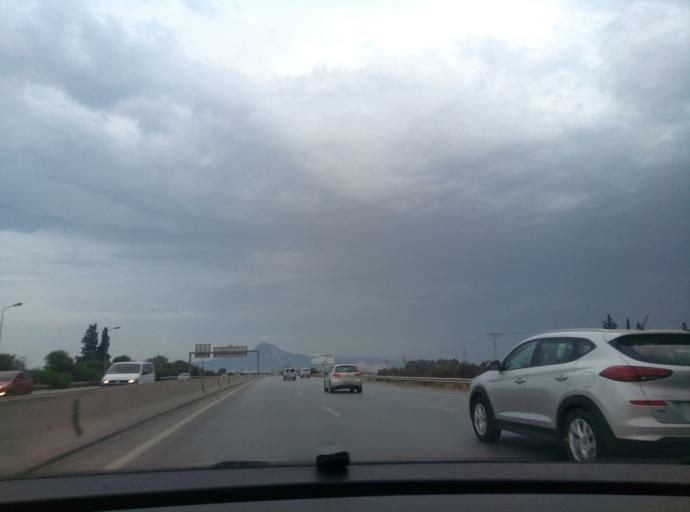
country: TN
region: Bin 'Arus
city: Ben Arous
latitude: 36.7277
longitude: 10.2481
